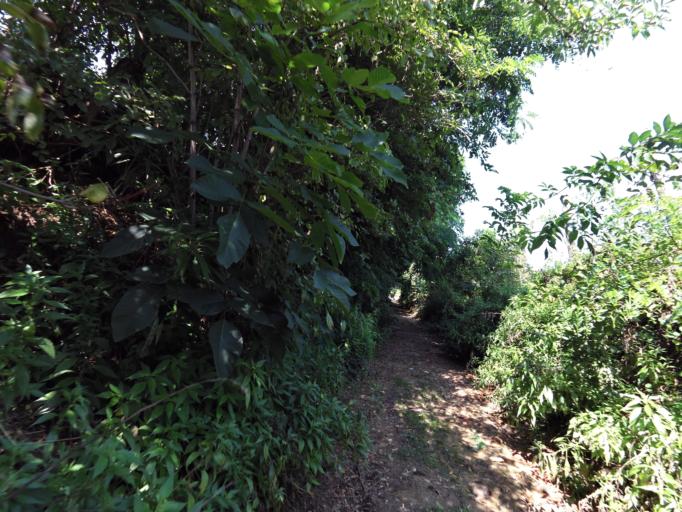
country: HU
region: Zala
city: Vonyarcvashegy
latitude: 46.8140
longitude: 17.3738
